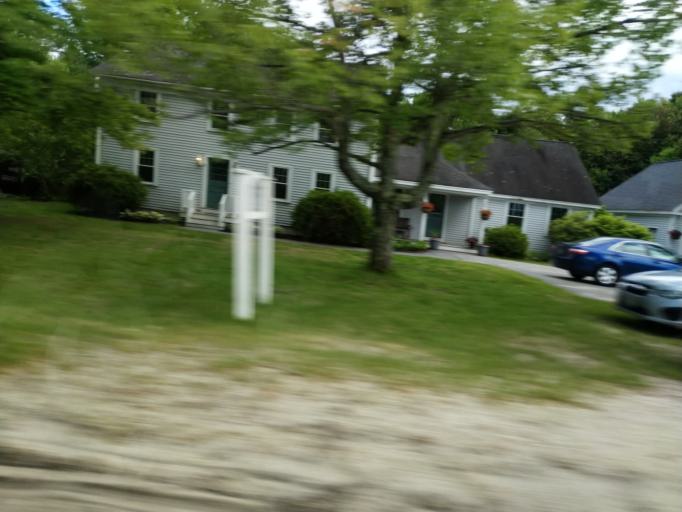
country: US
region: Maine
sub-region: Cumberland County
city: New Gloucester
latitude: 43.8862
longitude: -70.3197
